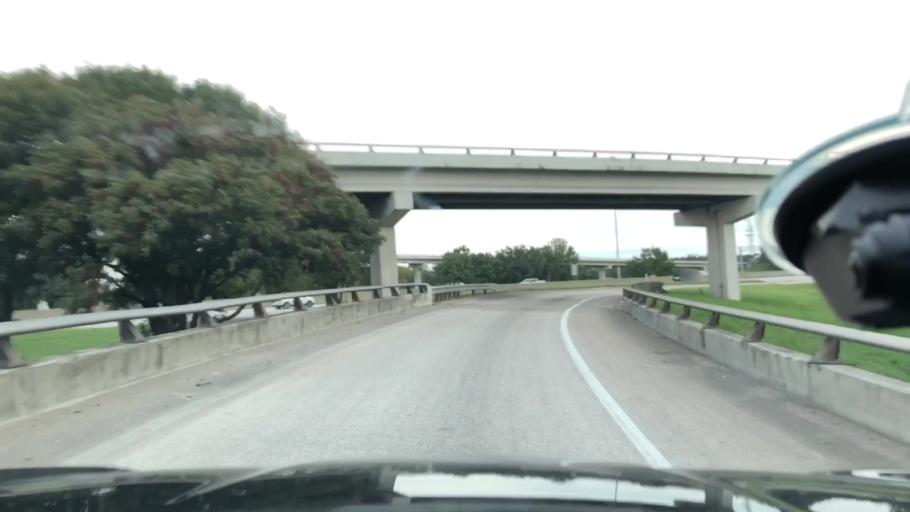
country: US
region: Texas
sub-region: Dallas County
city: DeSoto
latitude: 32.6415
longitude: -96.8225
